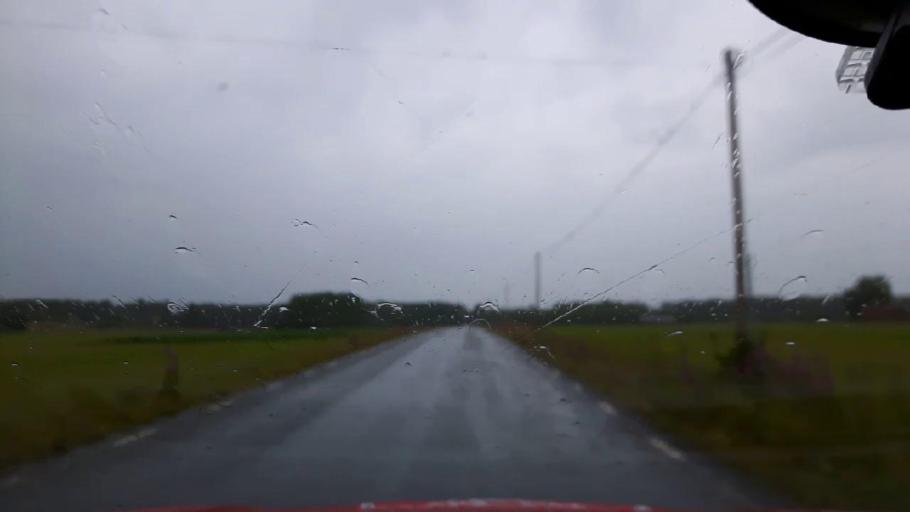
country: SE
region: Jaemtland
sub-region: OEstersunds Kommun
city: Brunflo
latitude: 62.9934
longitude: 14.7886
